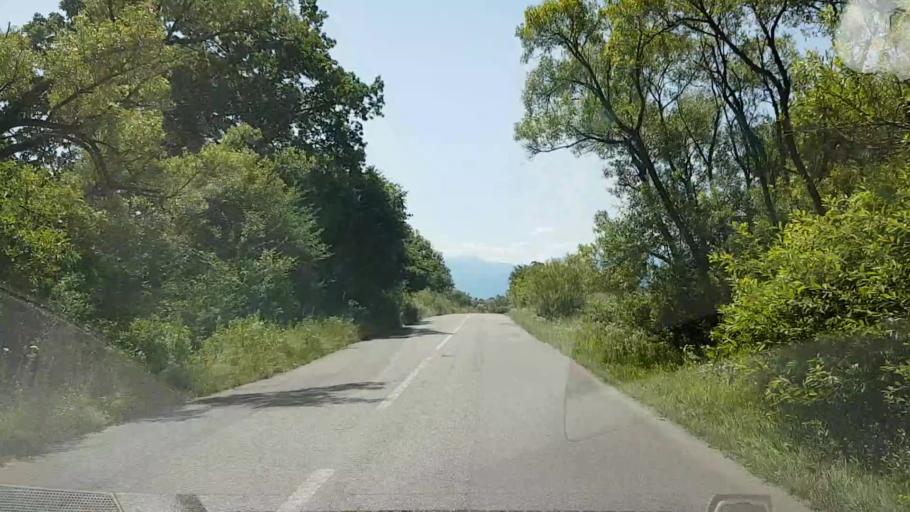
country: RO
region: Brasov
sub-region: Comuna Voila
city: Voila
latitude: 45.8657
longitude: 24.8249
